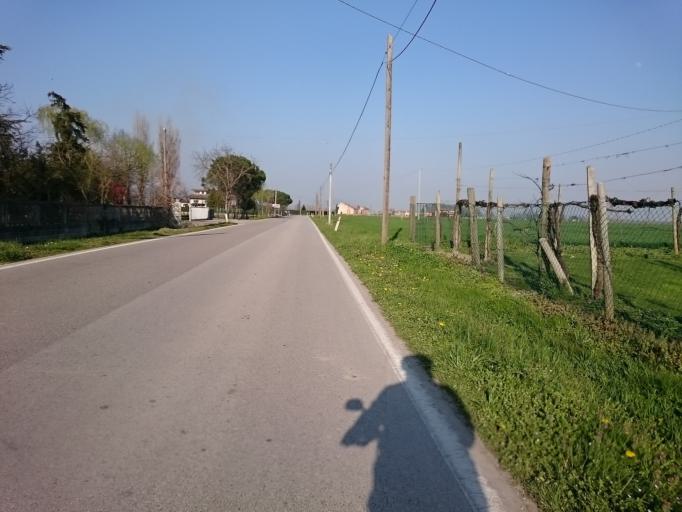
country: IT
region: Veneto
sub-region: Provincia di Padova
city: Carceri
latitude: 45.2005
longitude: 11.6261
